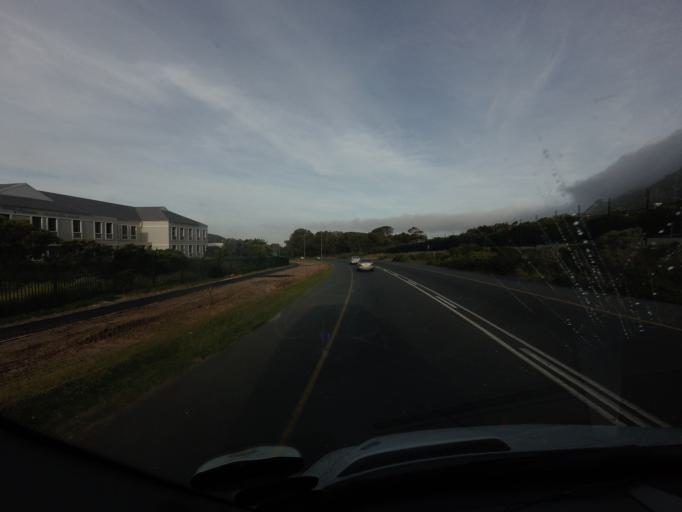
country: ZA
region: Western Cape
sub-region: City of Cape Town
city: Bergvliet
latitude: -34.0827
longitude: 18.4373
